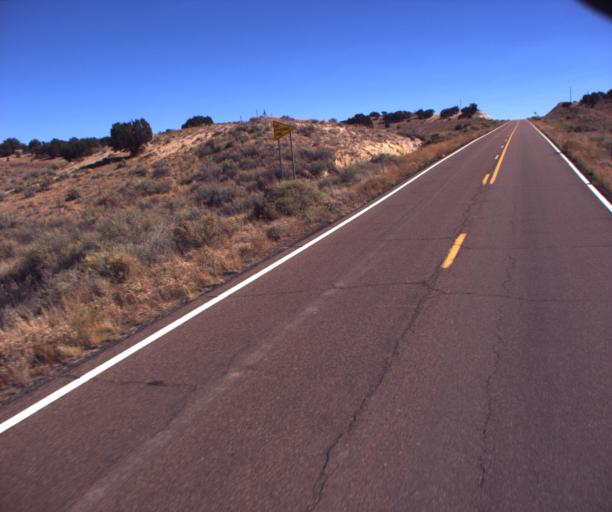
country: US
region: Arizona
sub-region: Navajo County
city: First Mesa
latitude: 35.7647
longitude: -109.9803
